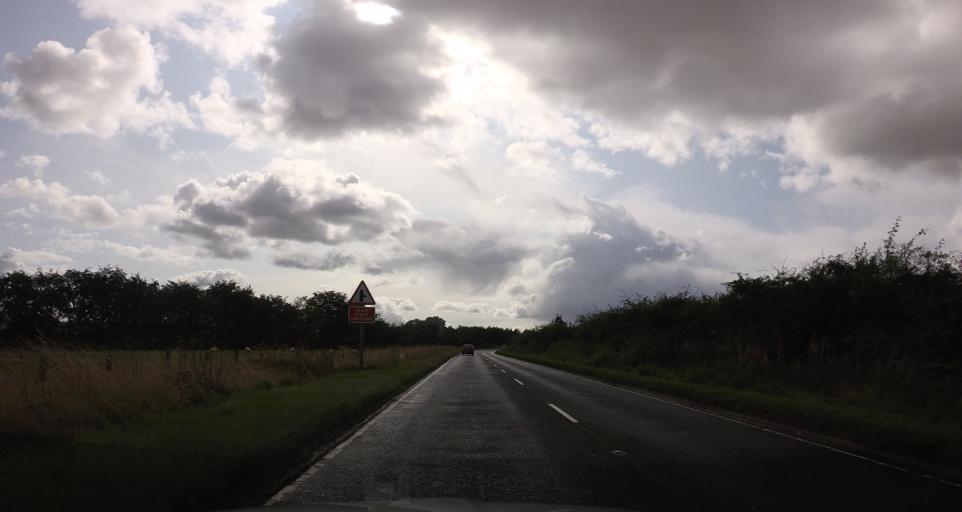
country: GB
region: Scotland
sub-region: Perth and Kinross
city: Kinross
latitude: 56.2058
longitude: -3.4665
